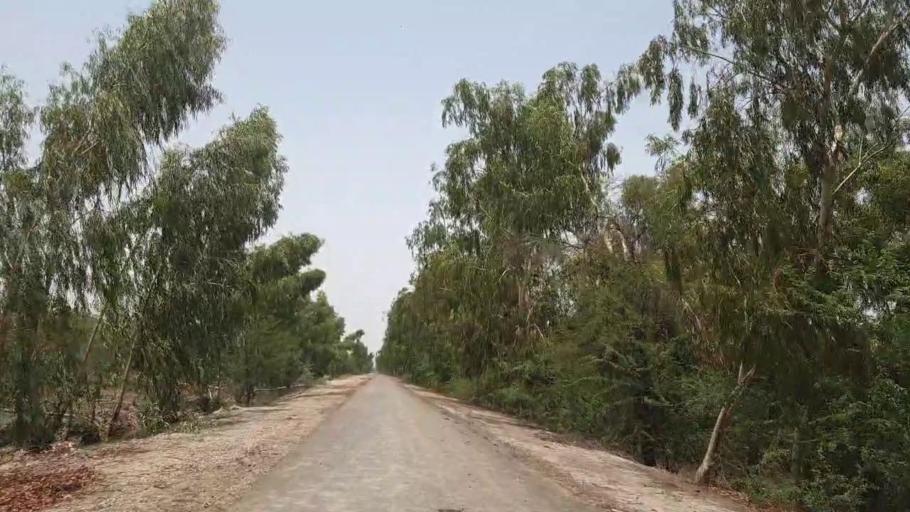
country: PK
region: Sindh
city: Sakrand
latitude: 26.0924
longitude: 68.2286
